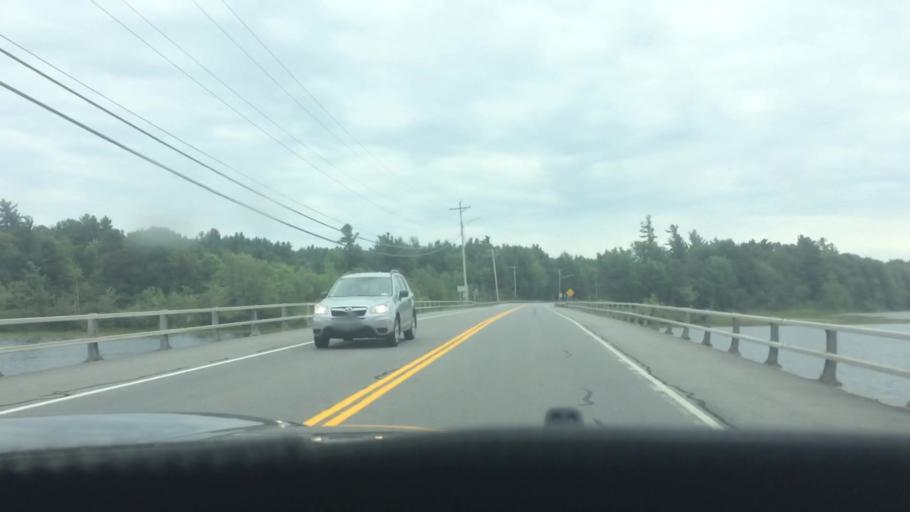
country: US
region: New York
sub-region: St. Lawrence County
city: Hannawa Falls
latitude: 44.5493
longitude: -74.9349
